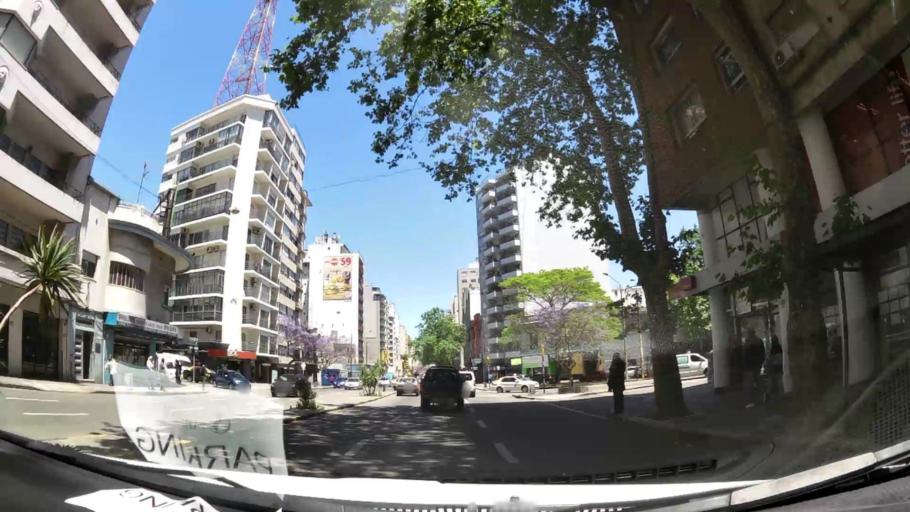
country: UY
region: Montevideo
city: Montevideo
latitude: -34.8979
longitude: -56.1656
